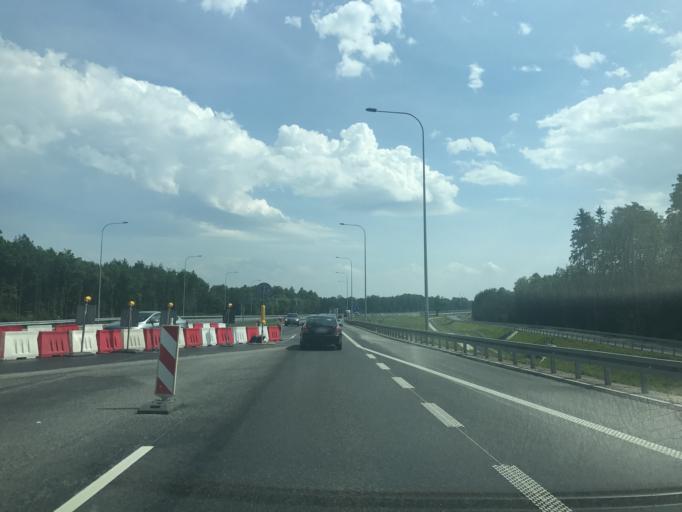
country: PL
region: Warmian-Masurian Voivodeship
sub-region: Powiat ostrodzki
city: Ostroda
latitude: 53.7281
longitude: 19.9390
